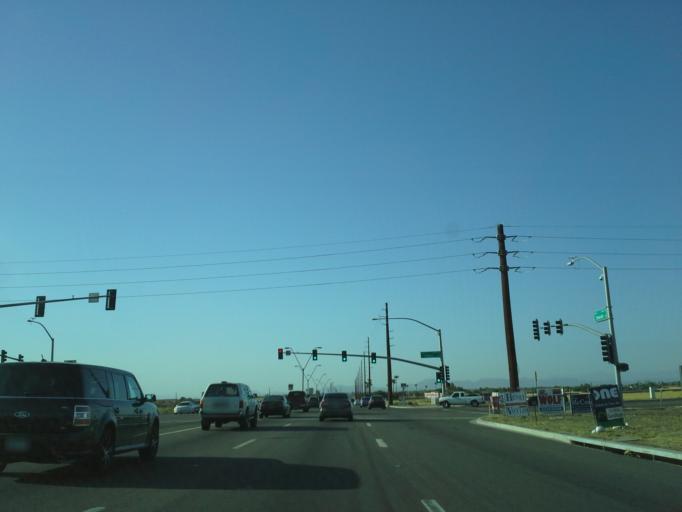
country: US
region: Arizona
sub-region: Maricopa County
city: Queen Creek
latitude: 33.2044
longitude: -111.6344
